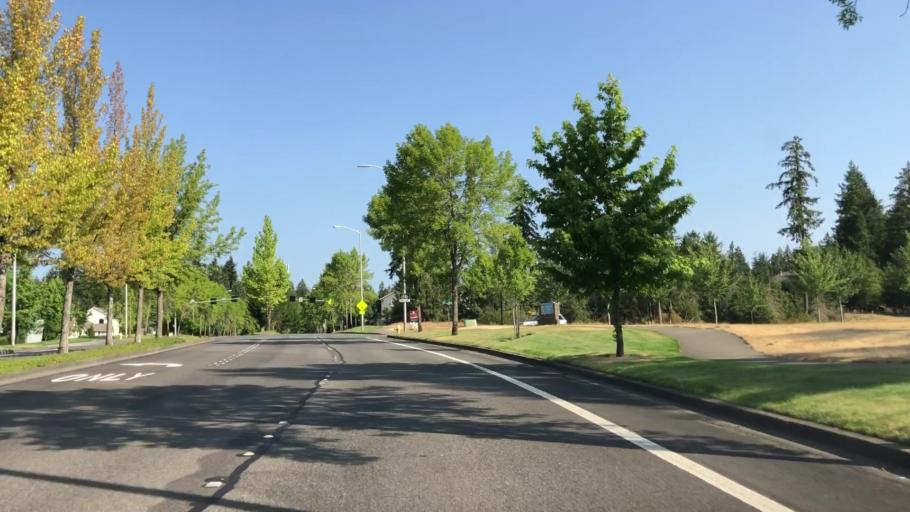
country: US
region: Washington
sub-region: Thurston County
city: Tanglewilde-Thompson Place
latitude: 47.0829
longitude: -122.7532
